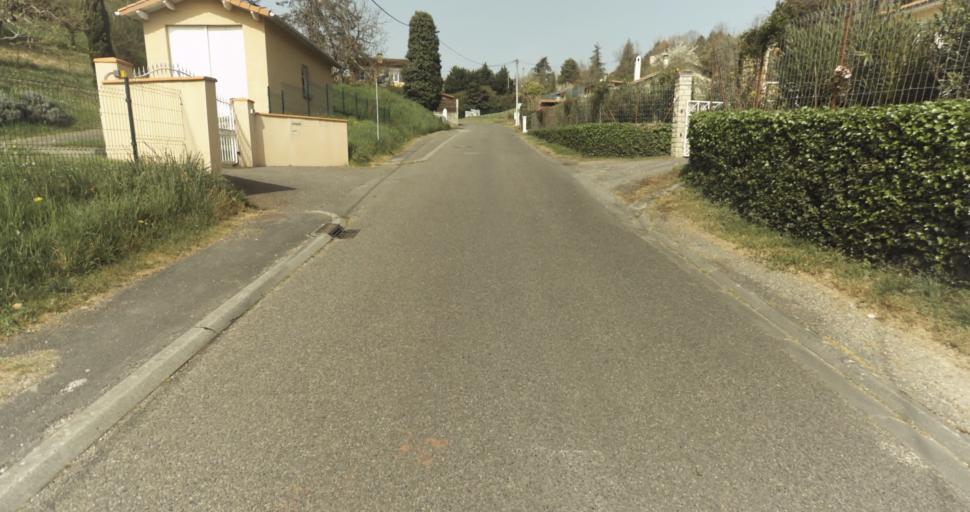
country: FR
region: Midi-Pyrenees
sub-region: Departement du Tarn-et-Garonne
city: Moissac
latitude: 44.1085
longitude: 1.0901
